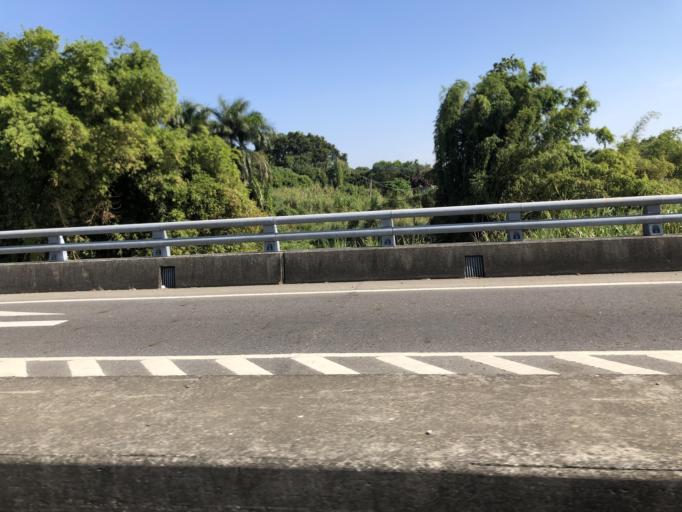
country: TW
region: Taiwan
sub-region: Tainan
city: Tainan
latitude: 23.0353
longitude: 120.3216
